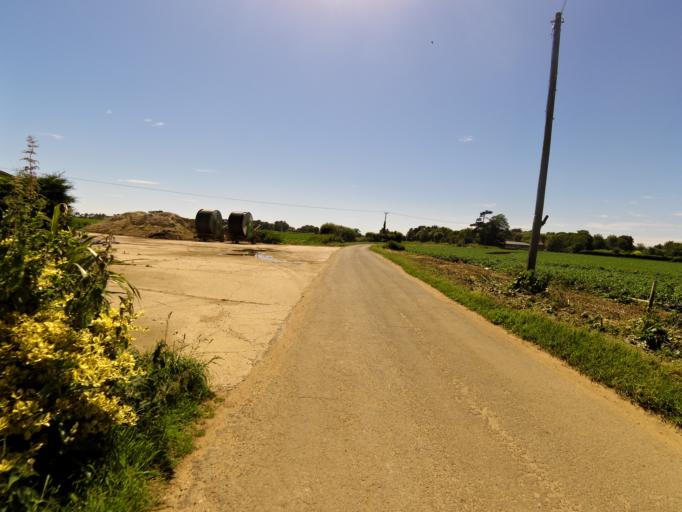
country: GB
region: England
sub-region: Suffolk
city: Felixstowe
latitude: 52.0083
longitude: 1.4247
